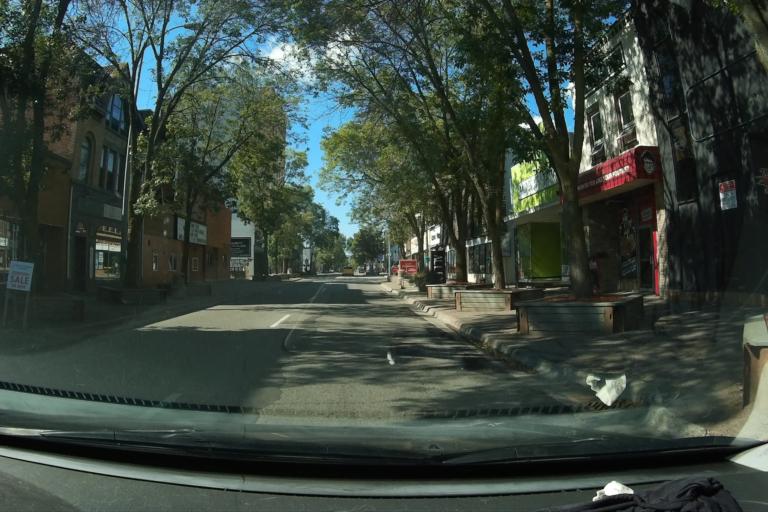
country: CA
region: Ontario
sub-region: Algoma
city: Sault Ste. Marie
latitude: 46.5083
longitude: -84.3288
